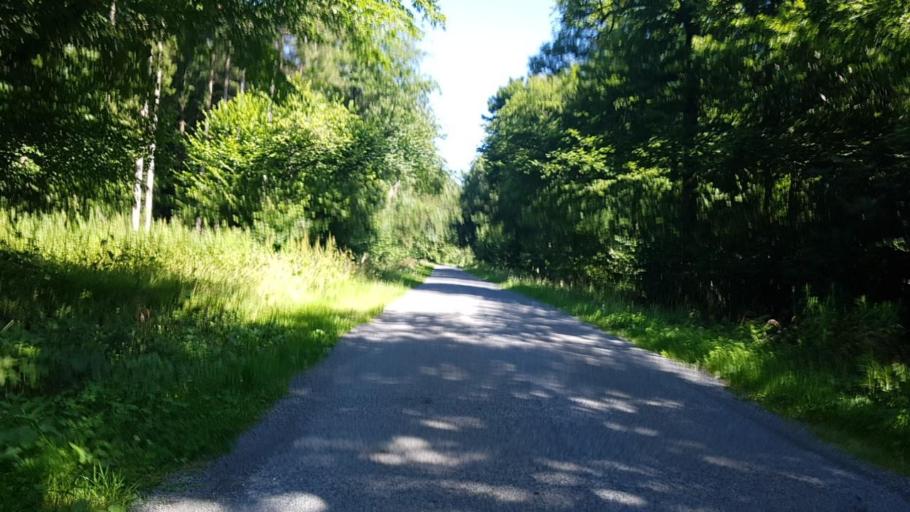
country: BE
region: Wallonia
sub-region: Province du Hainaut
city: Momignies
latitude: 50.0322
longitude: 4.2005
